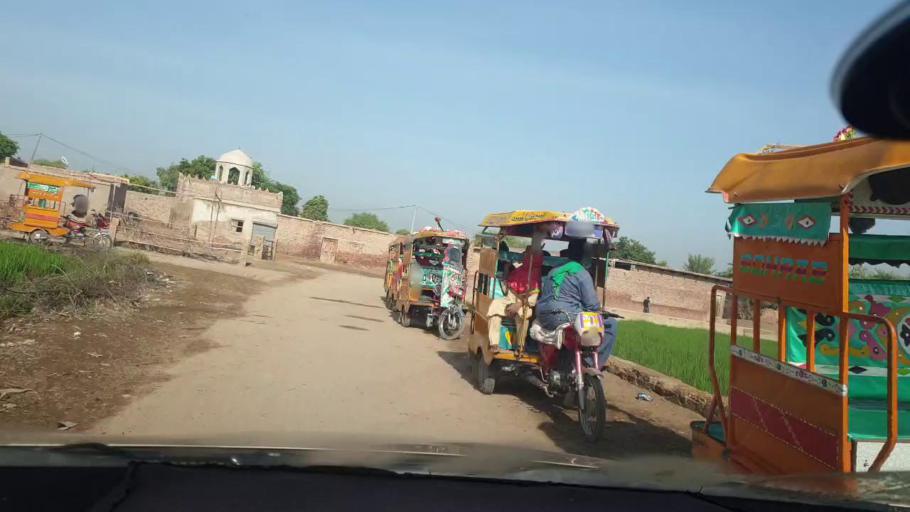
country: PK
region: Sindh
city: Kambar
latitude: 27.6608
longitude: 68.0145
